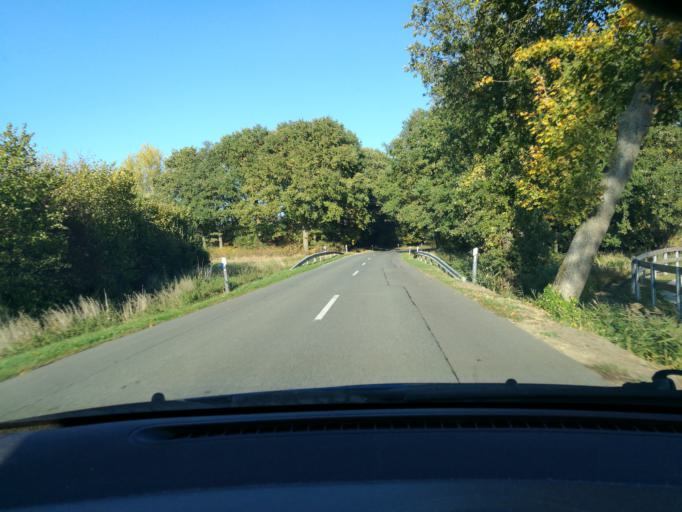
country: DE
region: Lower Saxony
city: Ludersburg
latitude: 53.3276
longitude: 10.5850
